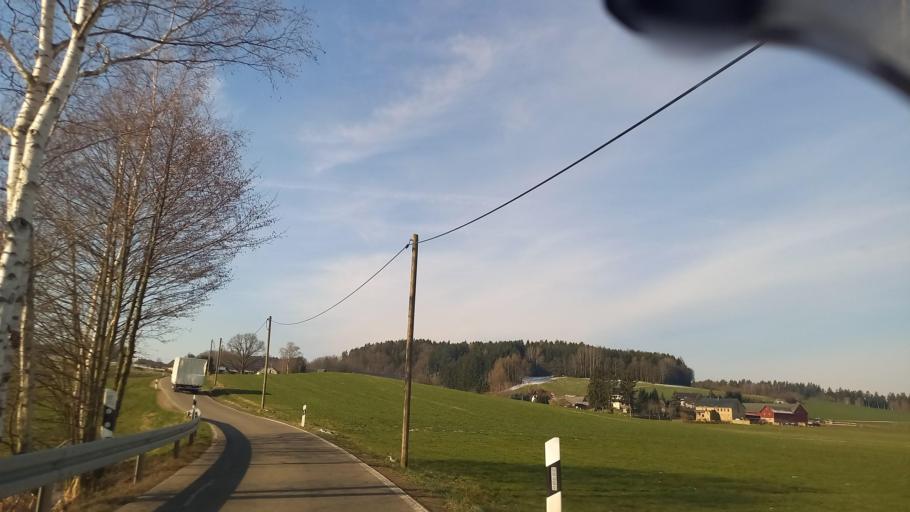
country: DE
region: Saxony
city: Kirchberg
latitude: 50.5927
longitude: 12.5214
